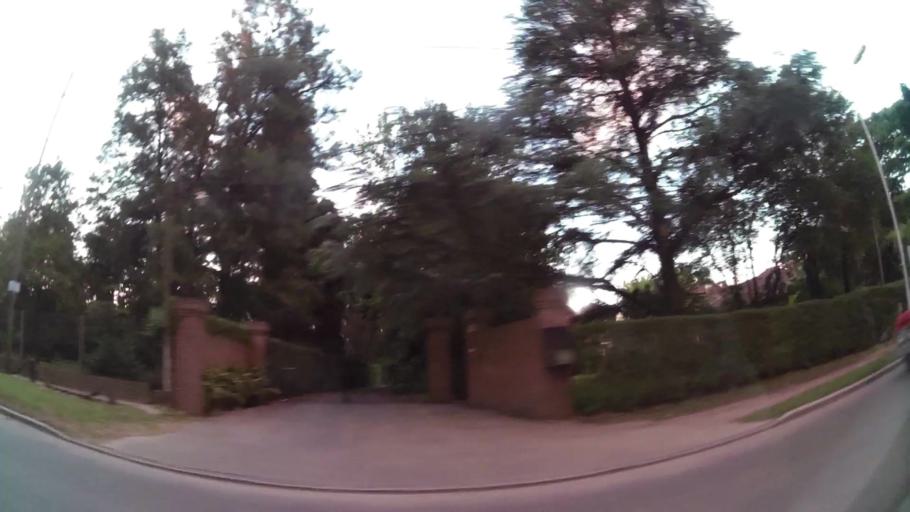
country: AR
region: Buenos Aires
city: Santa Catalina - Dique Lujan
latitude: -34.4763
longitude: -58.7695
